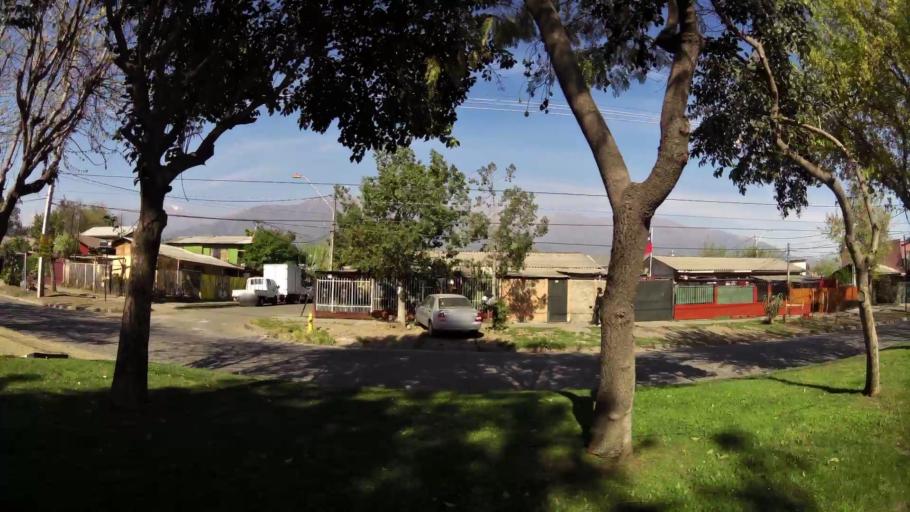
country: CL
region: Santiago Metropolitan
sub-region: Provincia de Santiago
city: Villa Presidente Frei, Nunoa, Santiago, Chile
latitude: -33.4630
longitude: -70.5658
